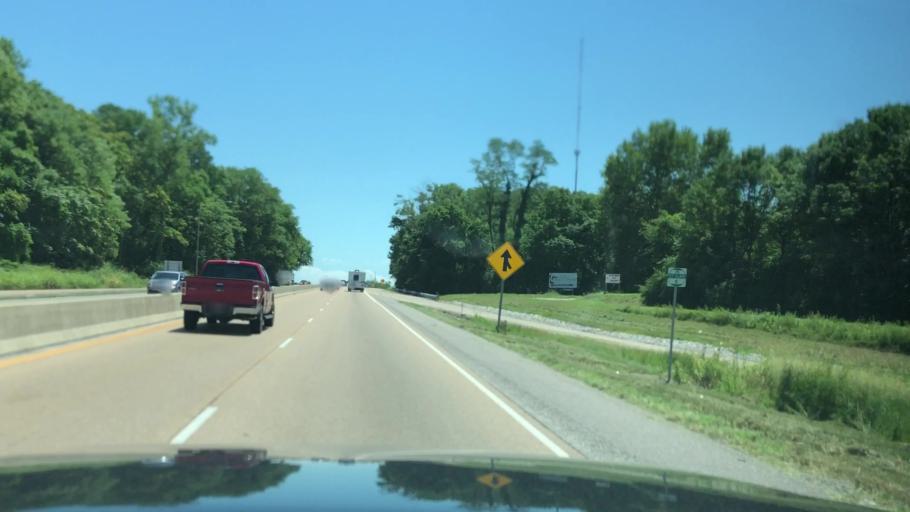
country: US
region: Illinois
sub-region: Saint Clair County
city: Alorton
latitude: 38.5661
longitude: -90.0899
